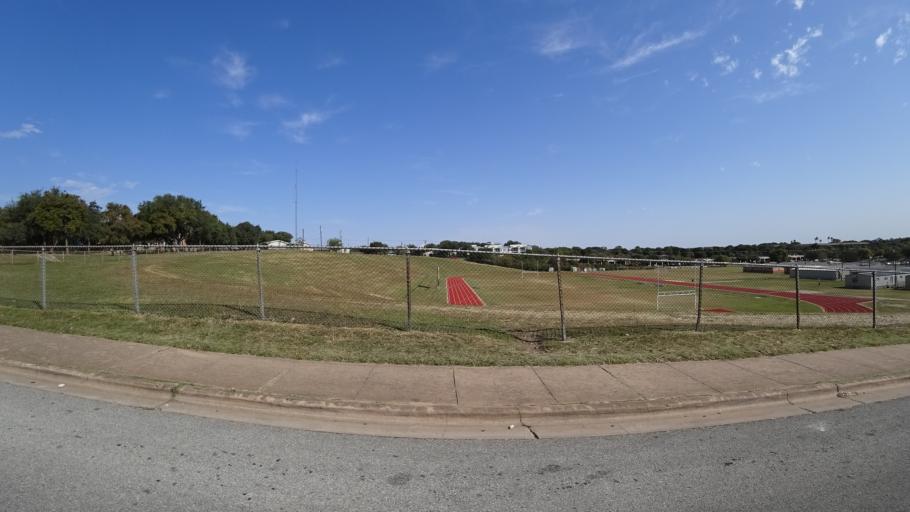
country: US
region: Texas
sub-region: Travis County
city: West Lake Hills
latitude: 30.3548
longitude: -97.7616
